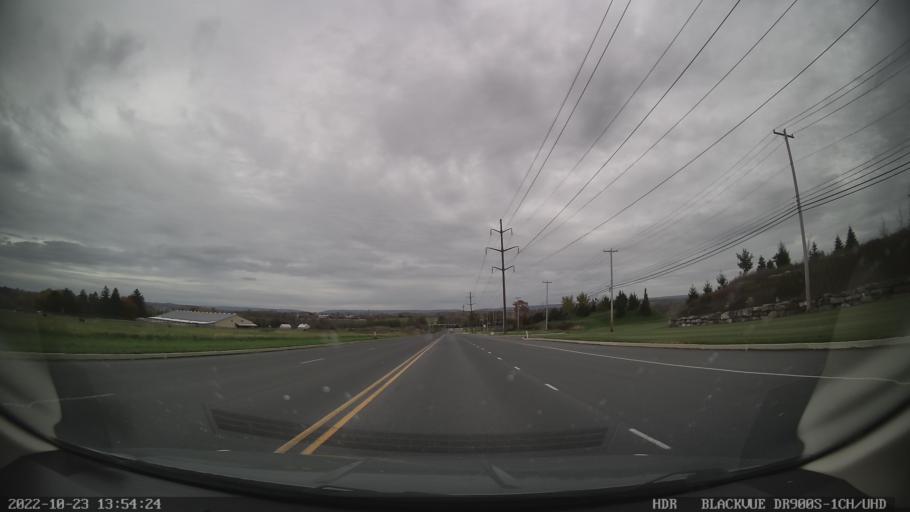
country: US
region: Pennsylvania
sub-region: Northampton County
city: North Catasauqua
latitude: 40.6705
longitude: -75.4577
